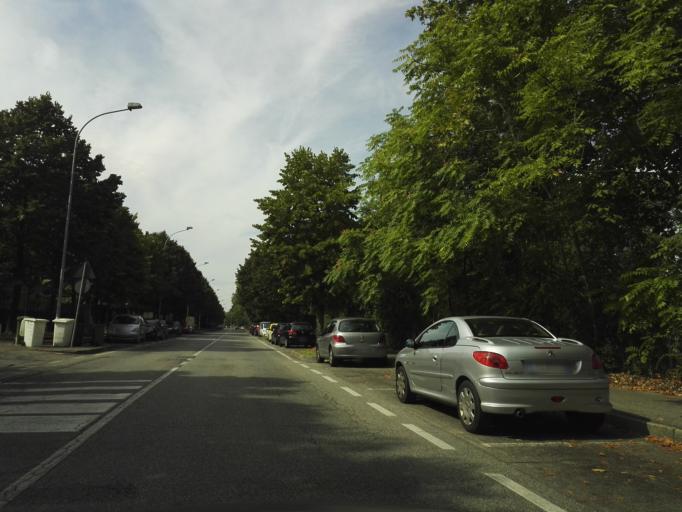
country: IT
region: Lombardy
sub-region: Citta metropolitana di Milano
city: Bettola-Zeloforomagno
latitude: 45.4285
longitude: 9.2999
